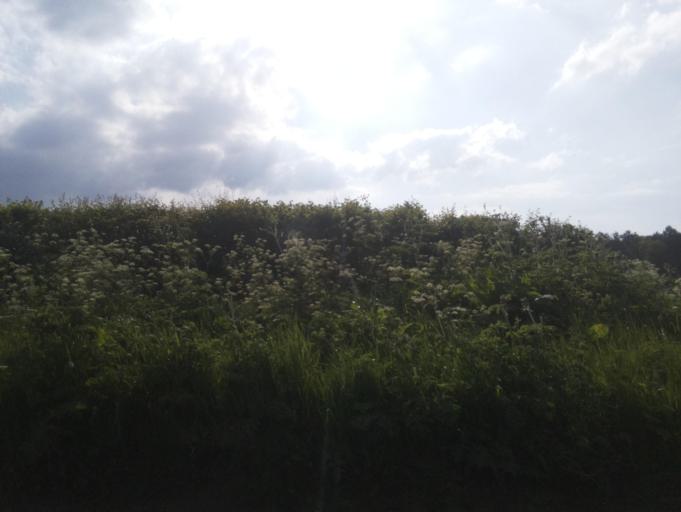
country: GB
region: England
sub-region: Wiltshire
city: Malmesbury
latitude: 51.5310
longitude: -2.0799
